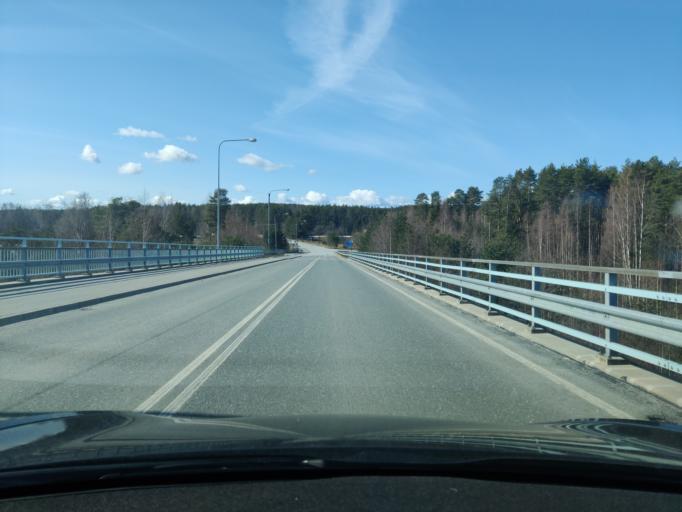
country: FI
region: Northern Savo
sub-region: Kuopio
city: Vehmersalmi
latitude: 62.7684
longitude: 28.0010
